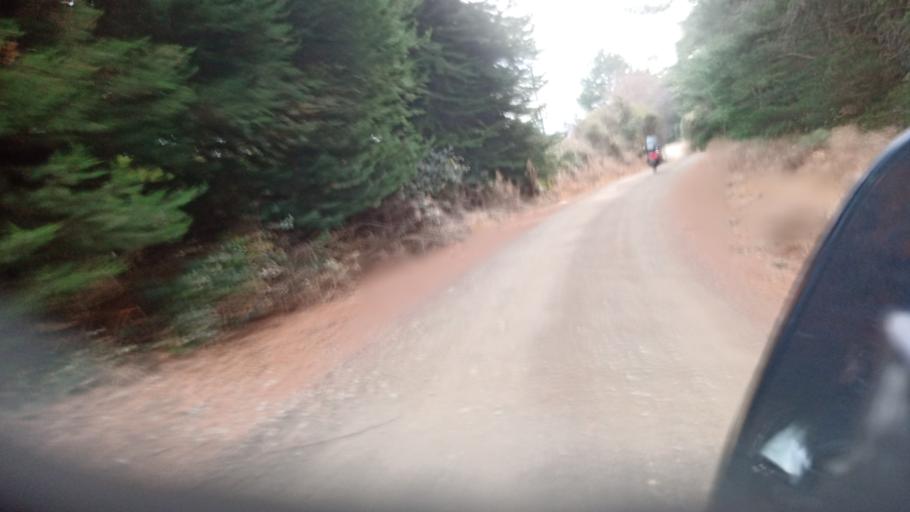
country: NZ
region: Bay of Plenty
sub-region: Opotiki District
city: Opotiki
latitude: -38.4733
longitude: 177.4408
